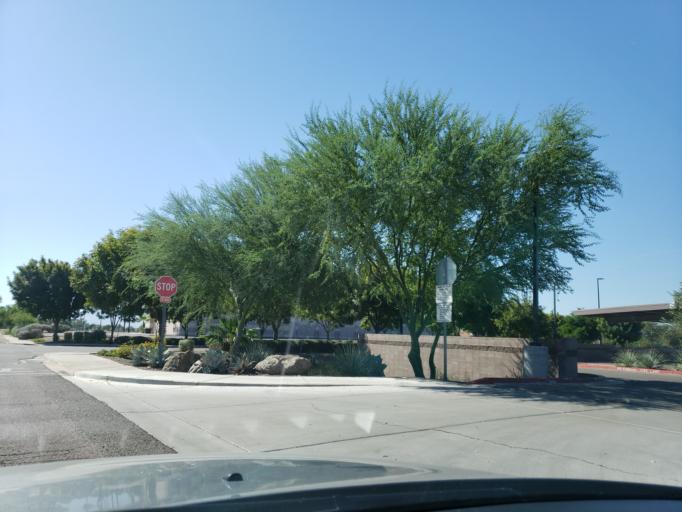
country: US
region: Arizona
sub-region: Maricopa County
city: Tolleson
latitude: 33.4782
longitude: -112.2282
